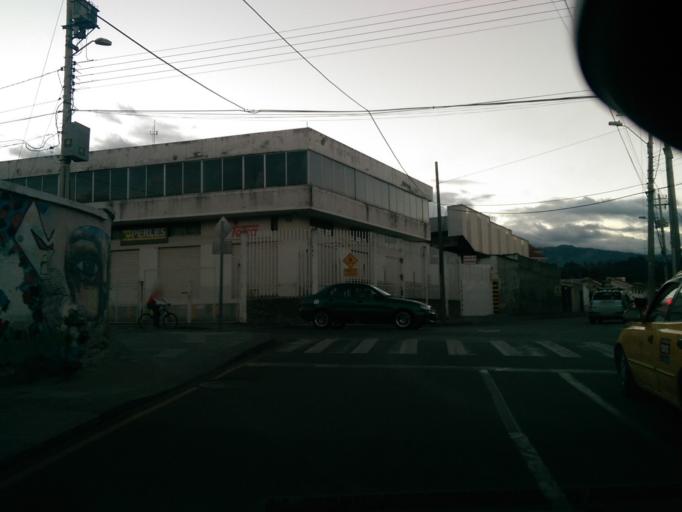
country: EC
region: Azuay
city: Cuenca
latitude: -2.9011
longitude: -79.0148
